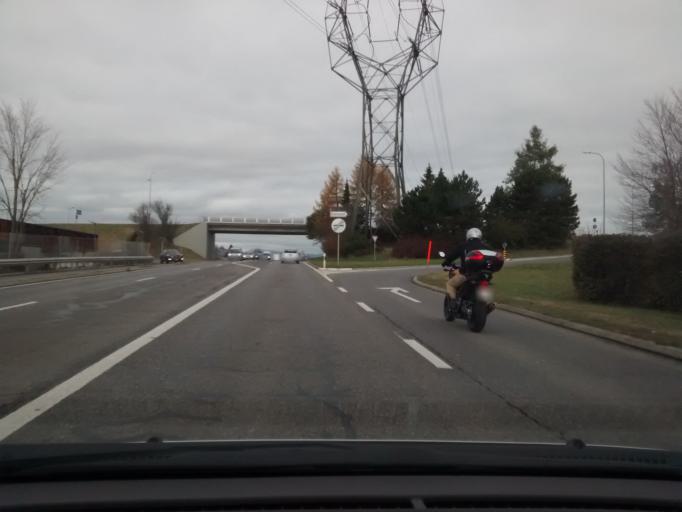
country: CH
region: Vaud
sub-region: Lausanne District
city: Romanel
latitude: 46.5594
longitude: 6.6140
